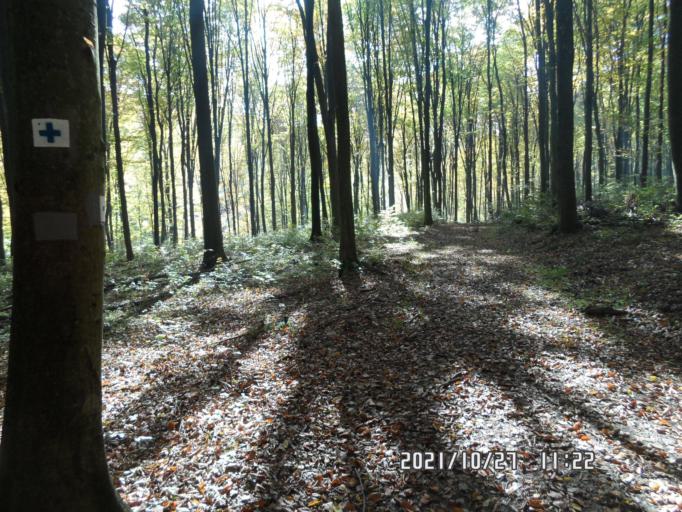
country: HU
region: Zala
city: Letenye
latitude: 46.5096
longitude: 16.7163
